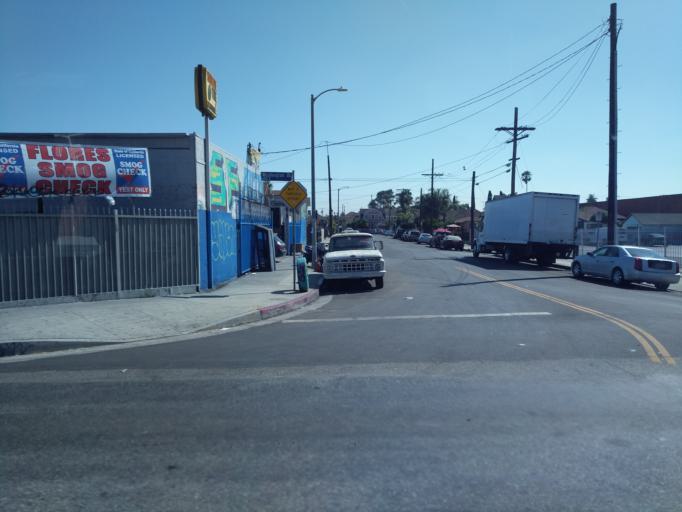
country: US
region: California
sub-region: Los Angeles County
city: Los Angeles
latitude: 34.0279
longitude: -118.2586
